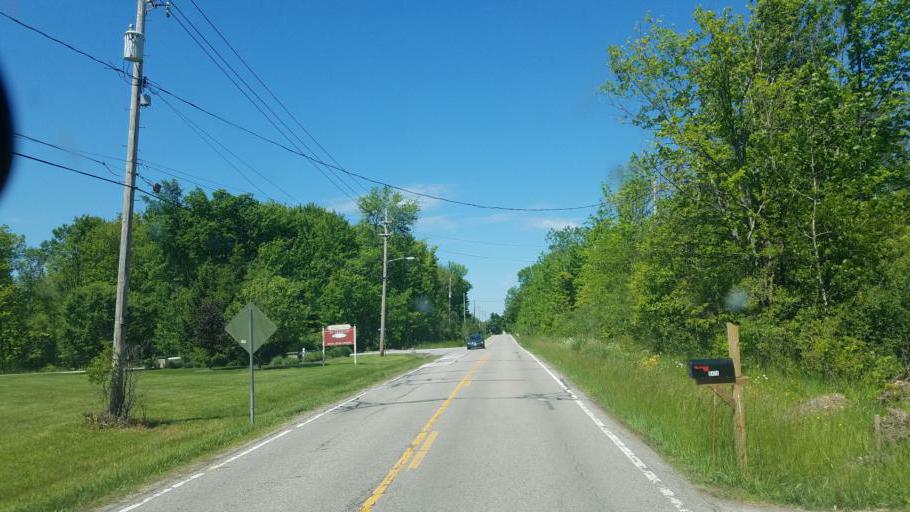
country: US
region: Ohio
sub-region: Geauga County
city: Bainbridge
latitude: 41.3695
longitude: -81.3040
